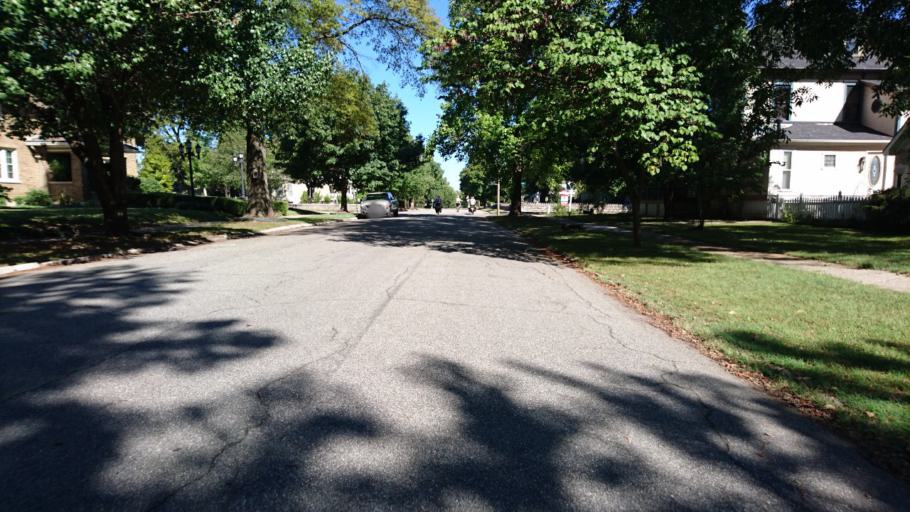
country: US
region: Missouri
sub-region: Jasper County
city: Joplin
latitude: 37.0884
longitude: -94.5201
